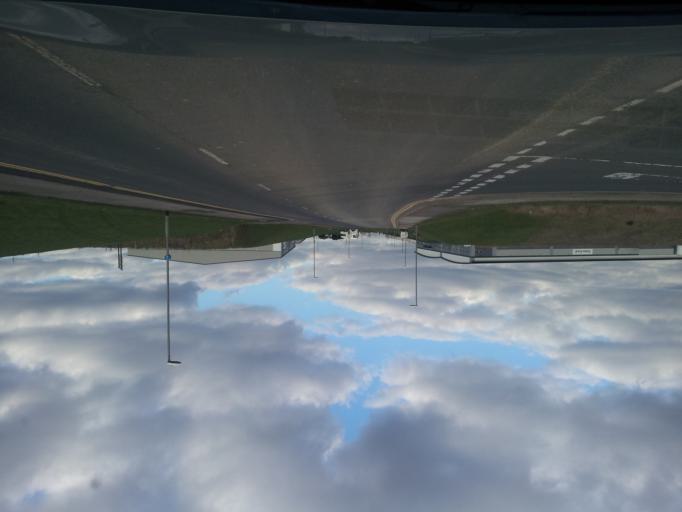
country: GB
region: England
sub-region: Derbyshire
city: Pinxton
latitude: 53.1085
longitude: -1.3027
